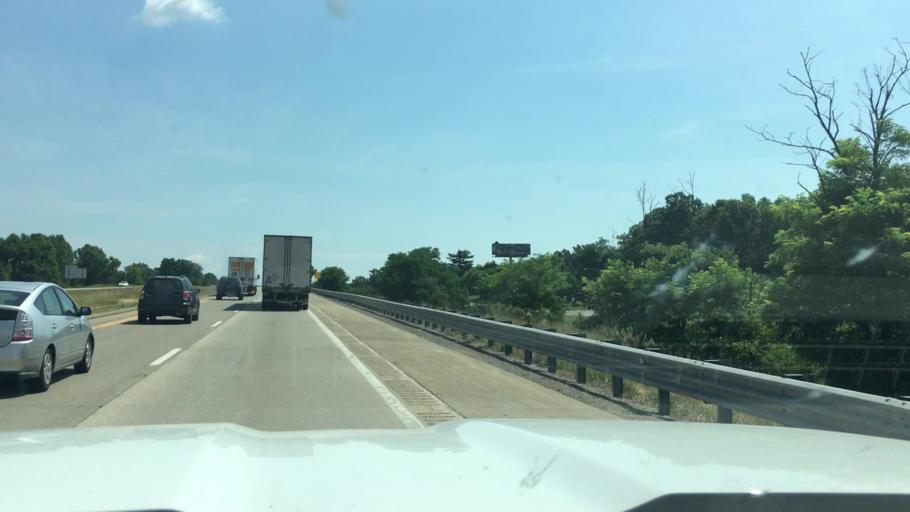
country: US
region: Michigan
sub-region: Shiawassee County
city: Laingsburg
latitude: 42.8049
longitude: -84.3278
